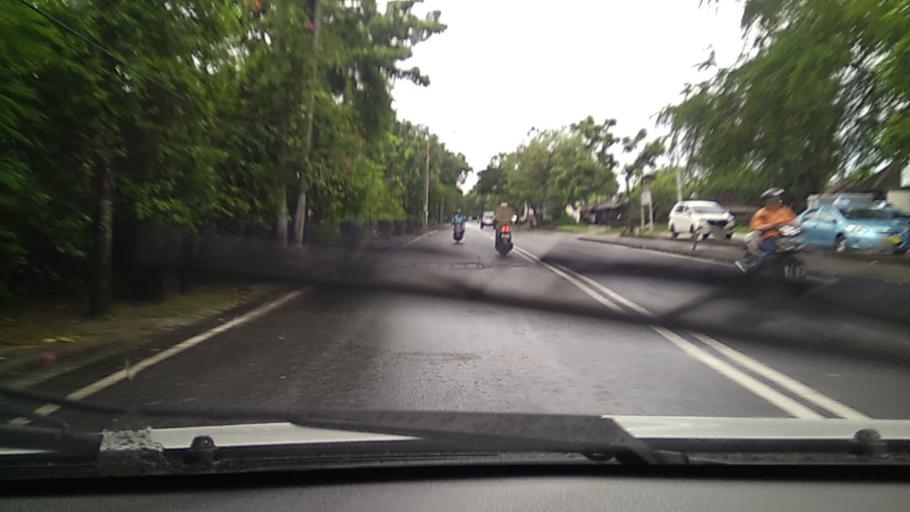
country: ID
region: Bali
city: Bualu
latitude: -8.7902
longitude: 115.2212
